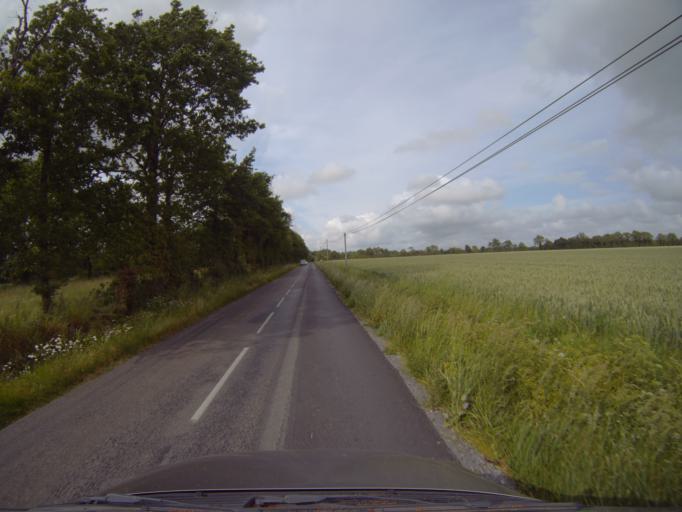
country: FR
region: Pays de la Loire
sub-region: Departement de la Loire-Atlantique
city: La Limouziniere
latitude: 47.0215
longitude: -1.5582
